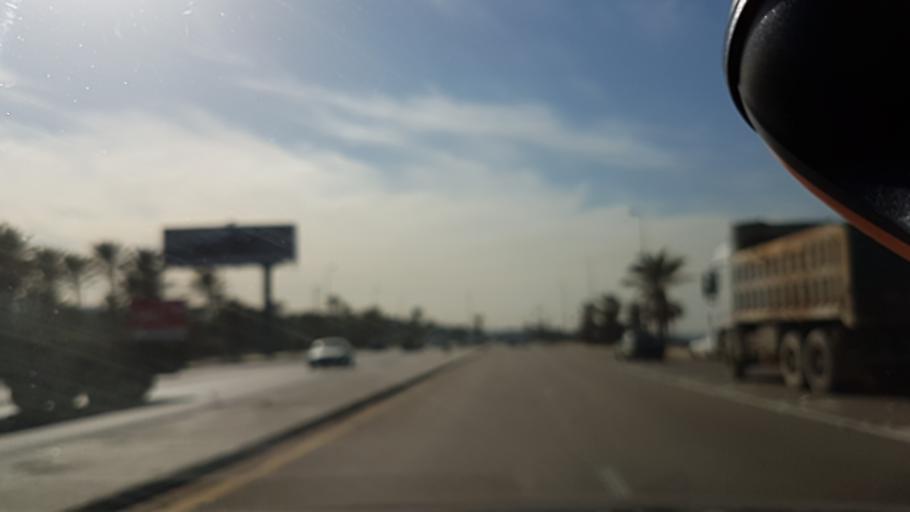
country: LB
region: Liban-Sud
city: Sidon
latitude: 33.5961
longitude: 35.3891
